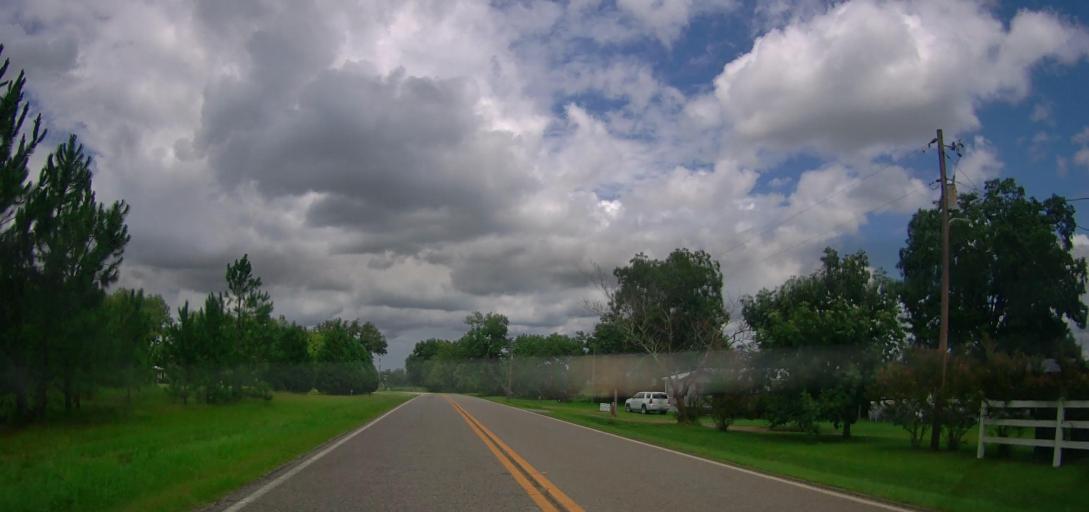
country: US
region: Georgia
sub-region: Wilcox County
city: Rochelle
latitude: 31.8930
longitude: -83.5535
